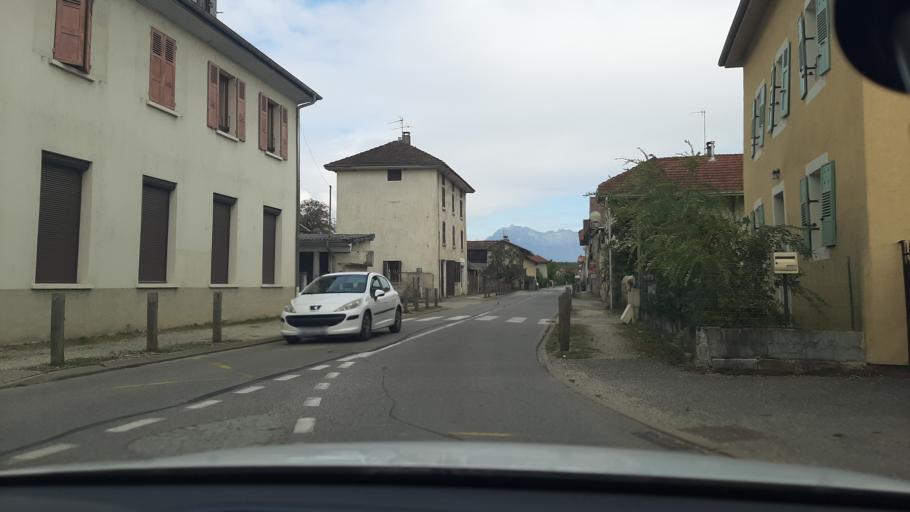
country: FR
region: Rhone-Alpes
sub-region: Departement de l'Isere
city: Pontcharra
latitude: 45.4469
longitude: 6.0371
